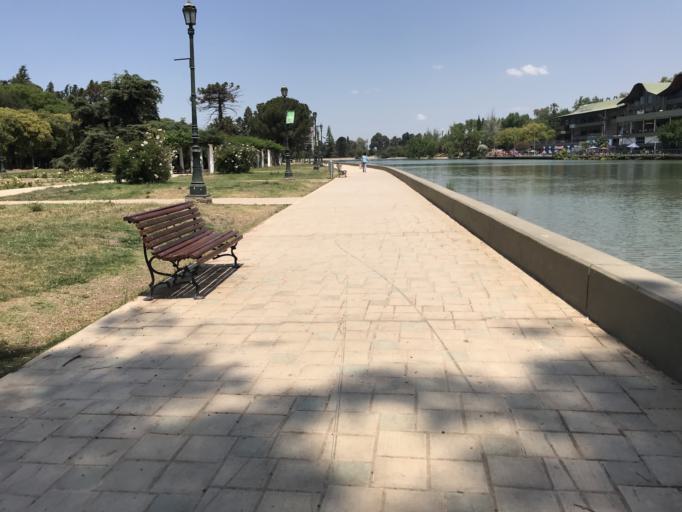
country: AR
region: Mendoza
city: Mendoza
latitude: -32.8918
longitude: -68.8669
